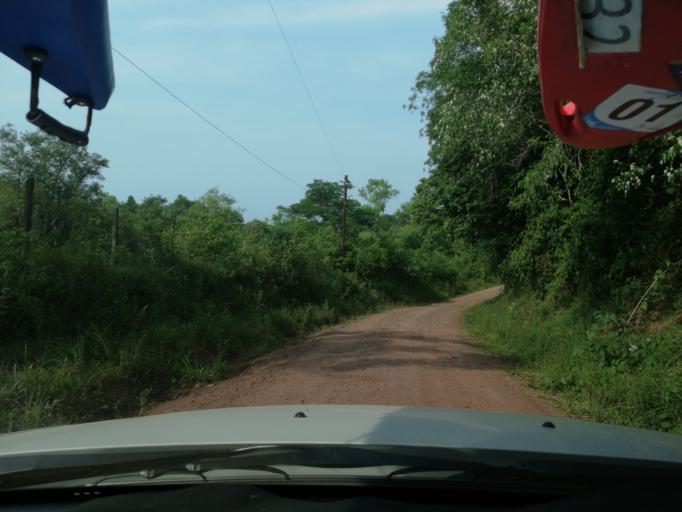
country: AR
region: Misiones
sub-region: Departamento de San Ignacio
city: San Ignacio
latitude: -27.3007
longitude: -55.5758
